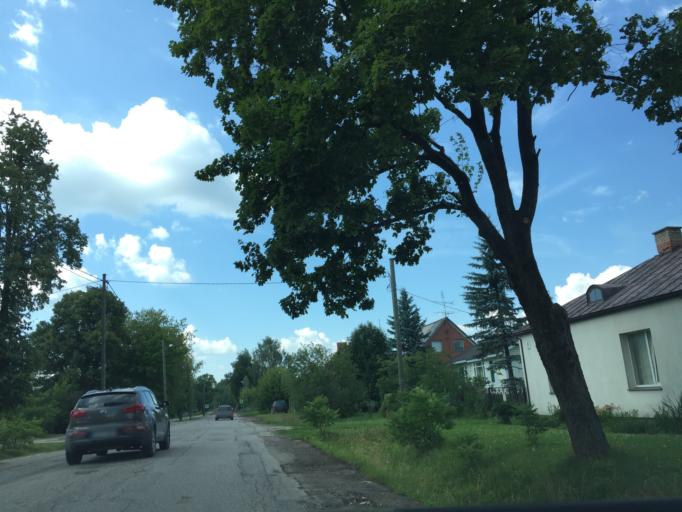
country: LV
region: Sigulda
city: Sigulda
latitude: 57.1514
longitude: 24.8617
